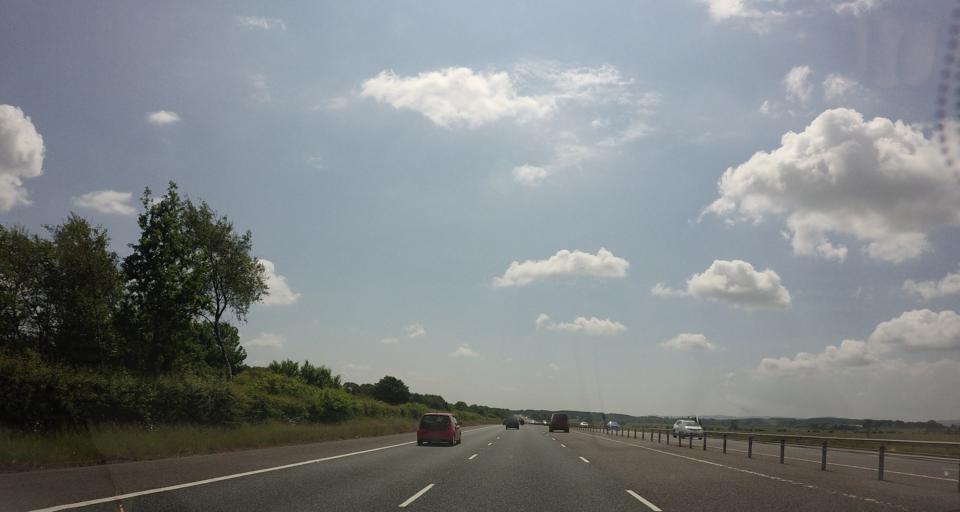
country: GB
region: Scotland
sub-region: Dumfries and Galloway
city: Lochmaben
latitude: 55.2001
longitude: -3.4111
